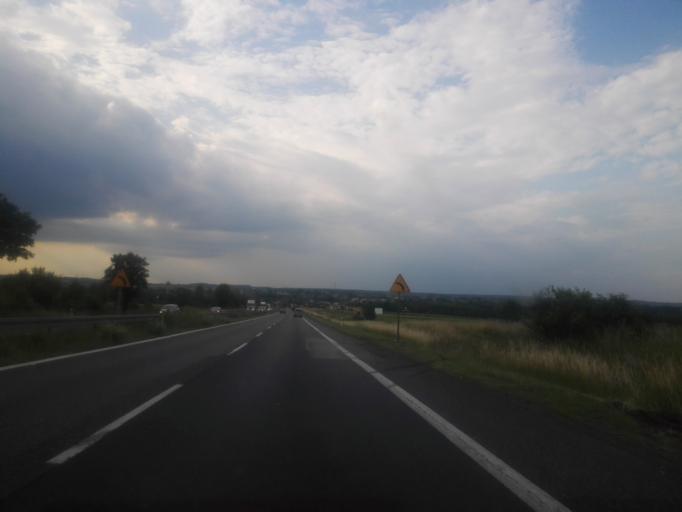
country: PL
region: Silesian Voivodeship
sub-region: Powiat myszkowski
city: Kozieglowy
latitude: 50.5841
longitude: 19.1639
